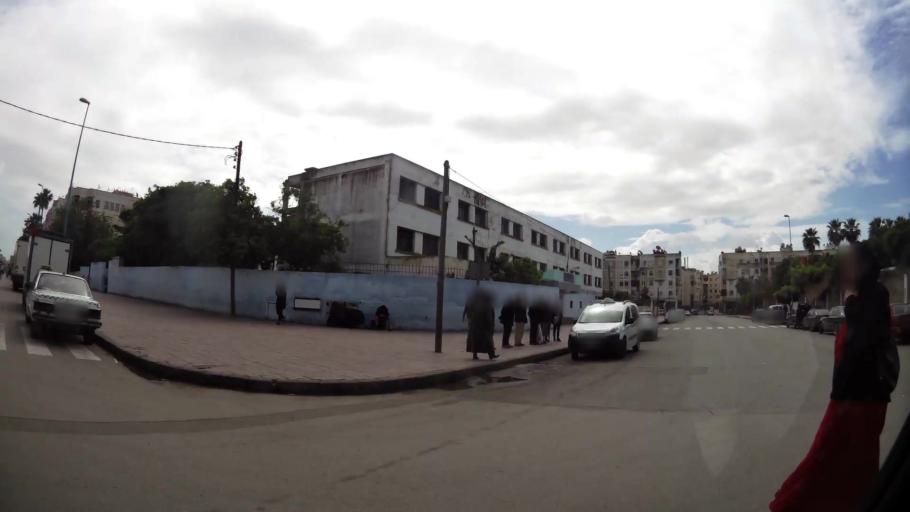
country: MA
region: Grand Casablanca
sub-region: Casablanca
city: Casablanca
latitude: 33.5694
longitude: -7.6828
